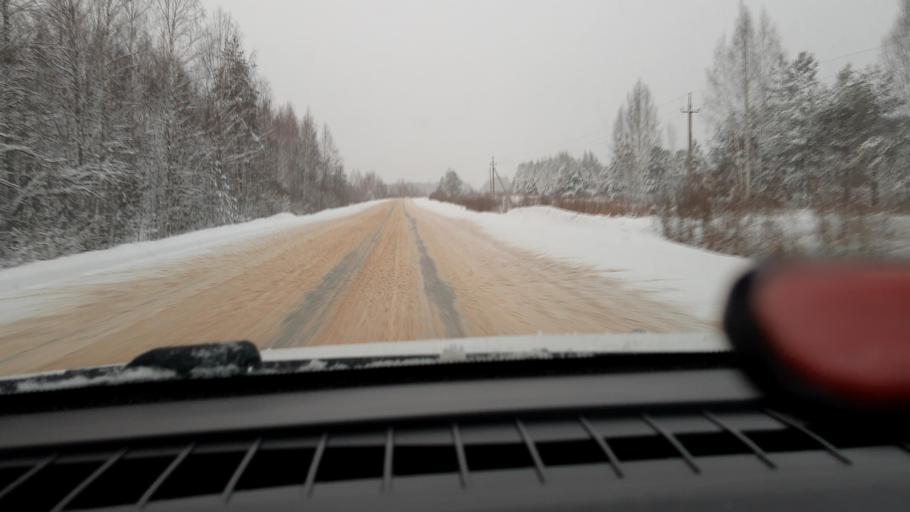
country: RU
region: Nizjnij Novgorod
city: Prudy
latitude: 57.3685
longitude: 46.1749
